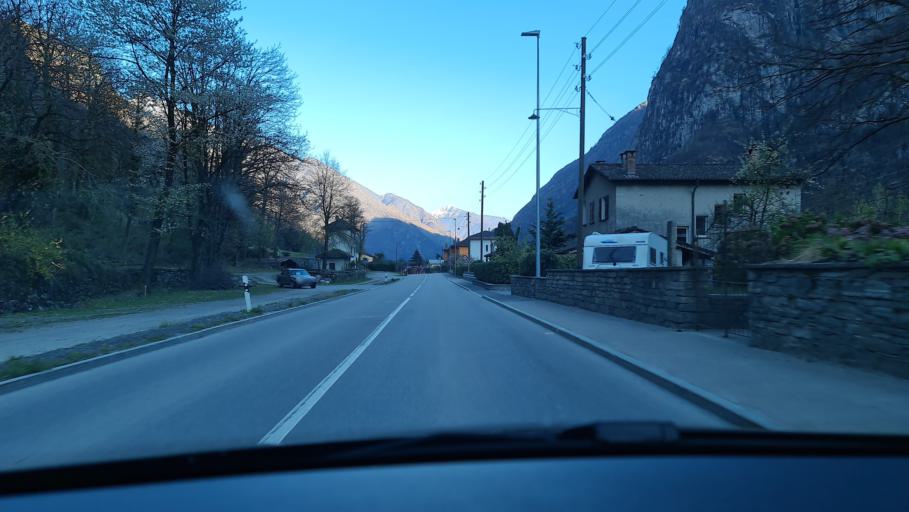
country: CH
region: Ticino
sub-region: Vallemaggia District
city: Cevio
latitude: 46.2987
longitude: 8.6252
